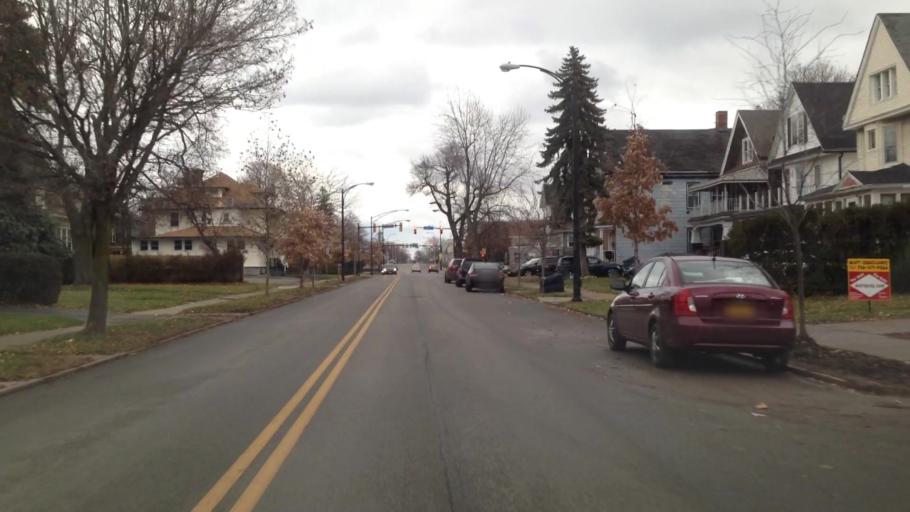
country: US
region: New York
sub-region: Erie County
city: Kenmore
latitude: 42.9403
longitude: -78.8407
